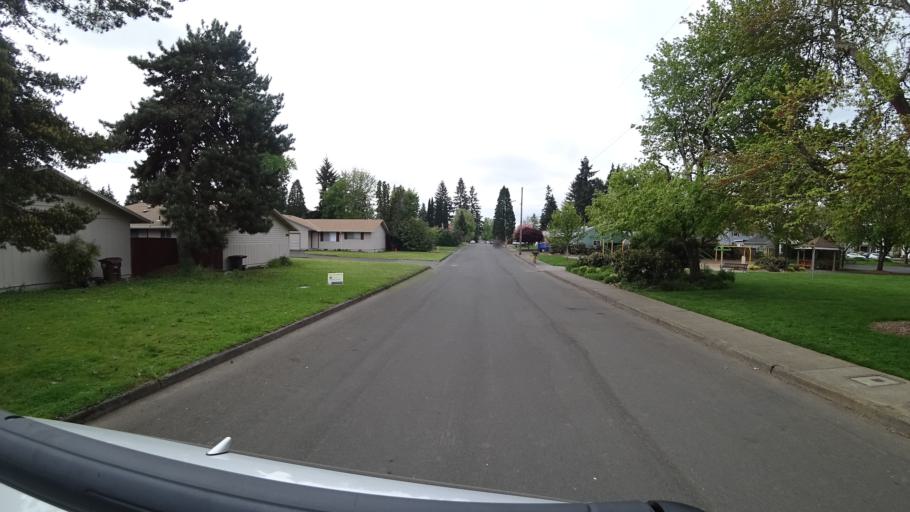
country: US
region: Oregon
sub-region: Washington County
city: Hillsboro
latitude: 45.5269
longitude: -122.9951
